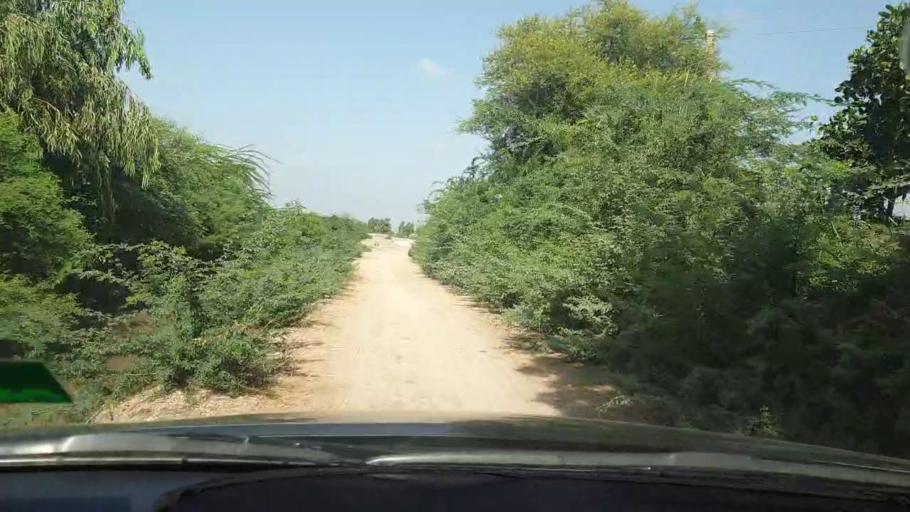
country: PK
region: Sindh
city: Tando Bago
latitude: 24.7818
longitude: 68.9422
